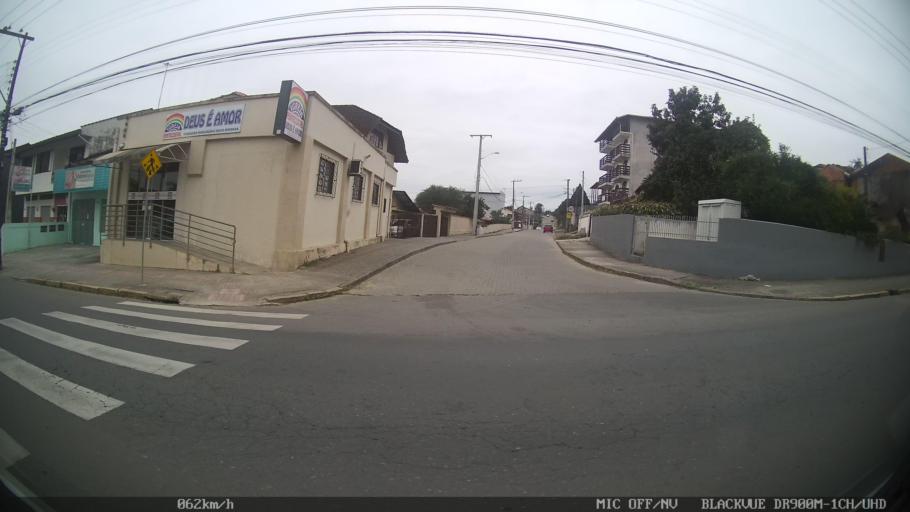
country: BR
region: Santa Catarina
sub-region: Joinville
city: Joinville
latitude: -26.3331
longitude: -48.8361
